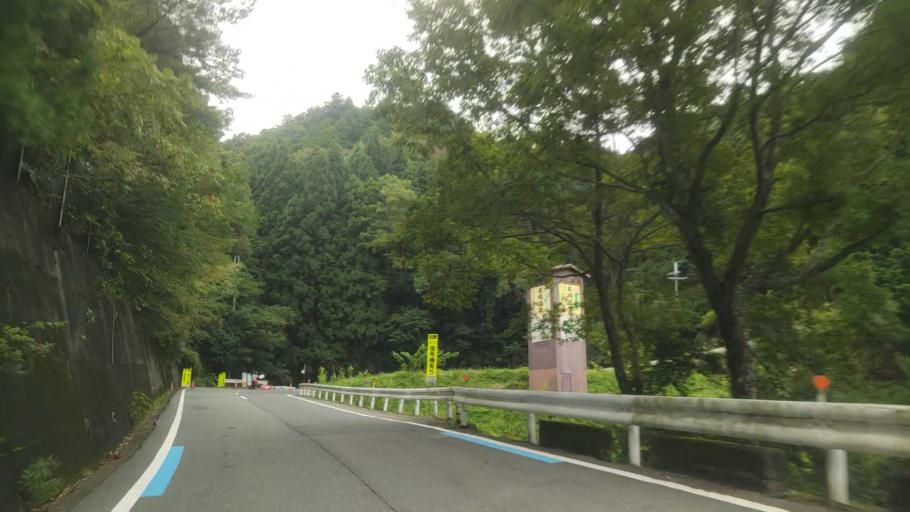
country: JP
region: Wakayama
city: Koya
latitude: 34.2172
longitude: 135.5377
